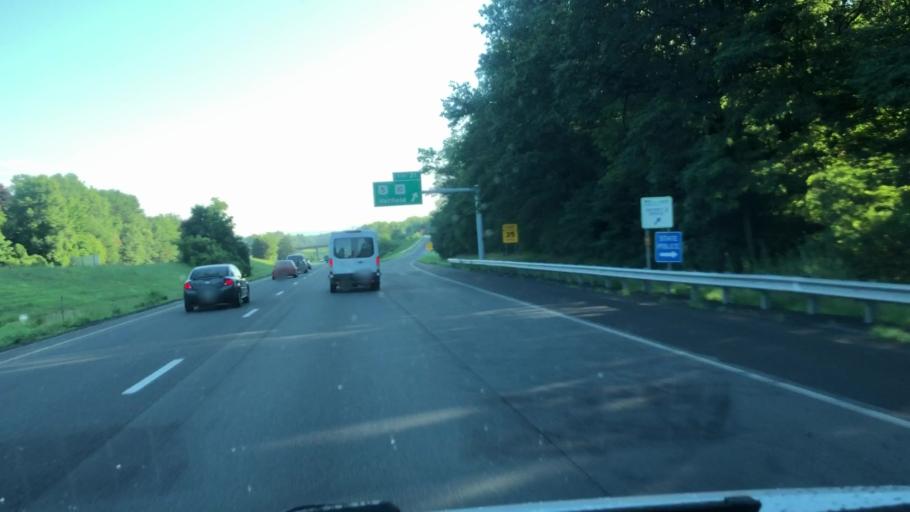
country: US
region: Massachusetts
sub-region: Hampshire County
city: Northampton
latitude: 42.3567
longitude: -72.6378
